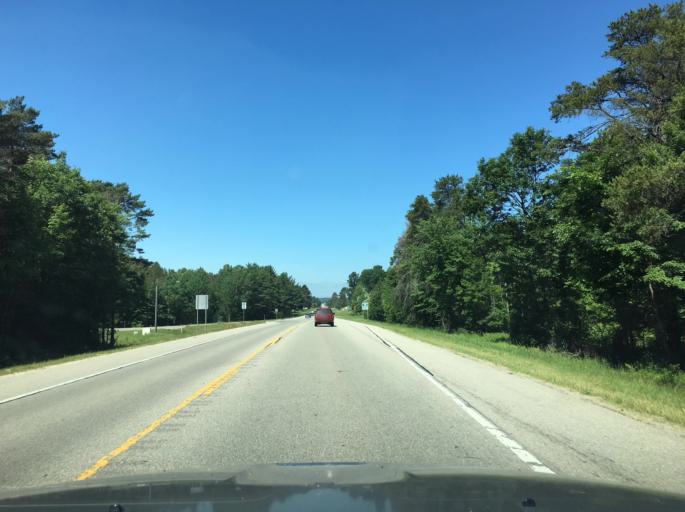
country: US
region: Michigan
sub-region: Osceola County
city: Reed City
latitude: 43.8725
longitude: -85.4428
